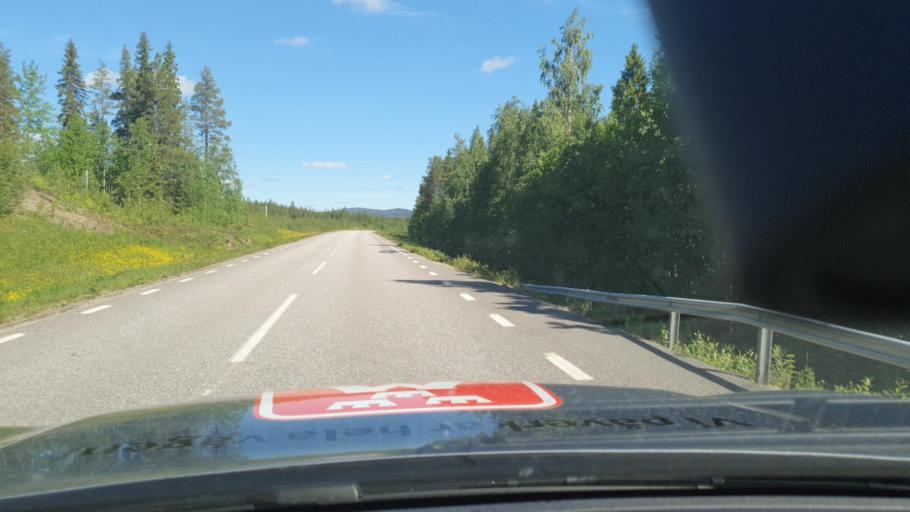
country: SE
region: Norrbotten
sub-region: Overkalix Kommun
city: OEverkalix
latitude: 66.7508
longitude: 22.6722
